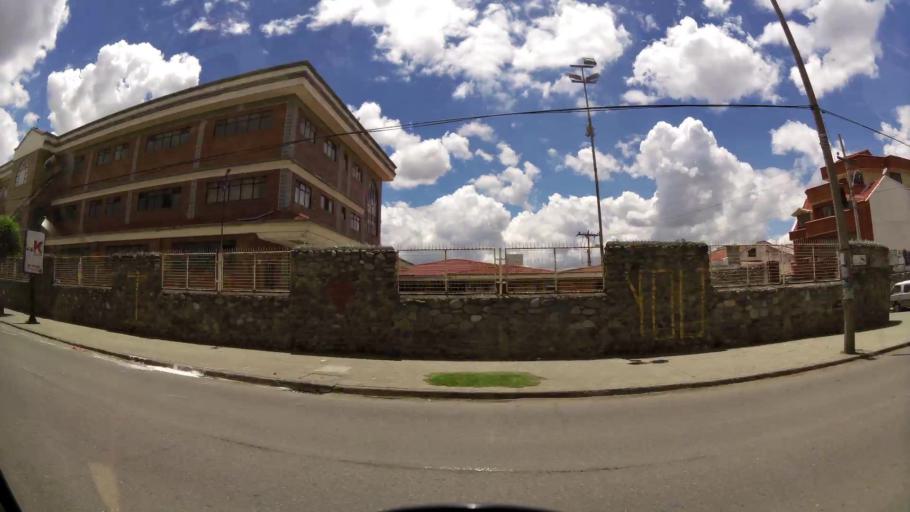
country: EC
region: Azuay
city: Cuenca
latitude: -2.8850
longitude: -79.0058
